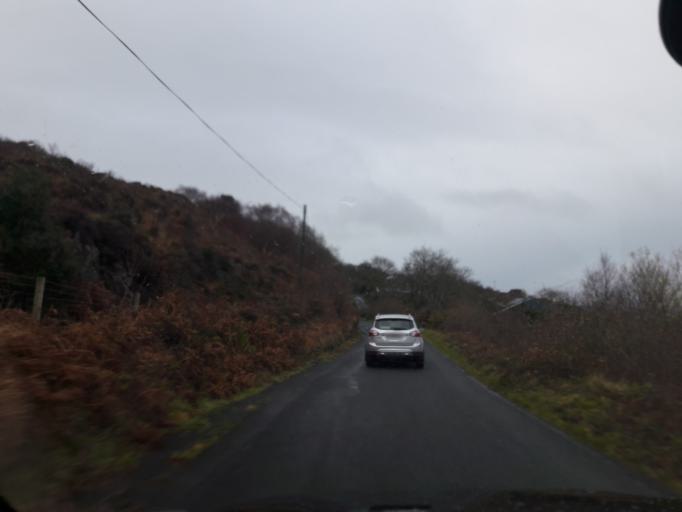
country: IE
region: Ulster
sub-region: County Donegal
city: Buncrana
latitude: 55.2314
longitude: -7.6174
